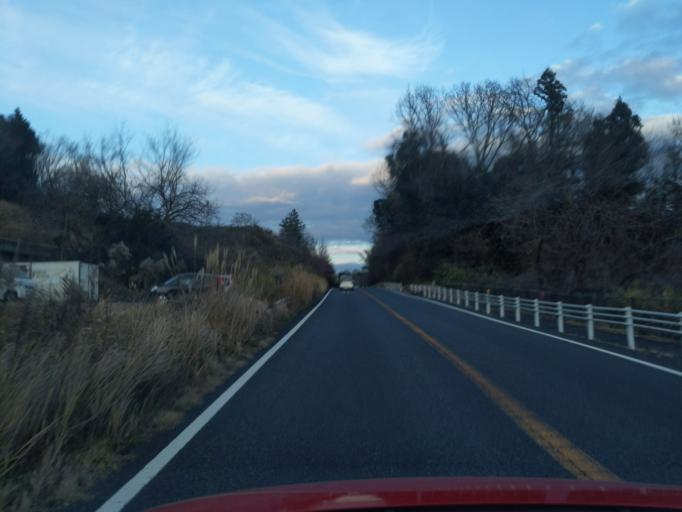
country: JP
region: Gifu
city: Mizunami
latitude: 35.4171
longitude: 137.3135
